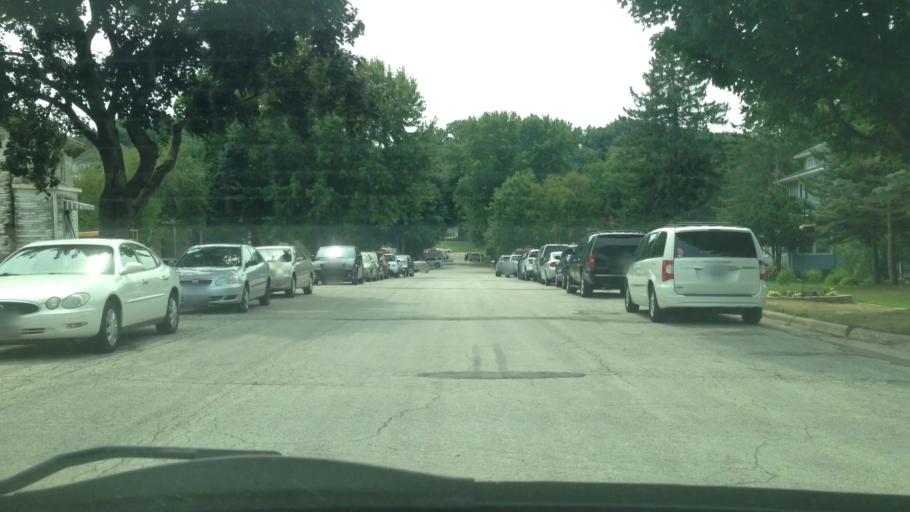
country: US
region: Minnesota
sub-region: Fillmore County
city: Preston
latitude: 43.7150
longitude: -91.9741
